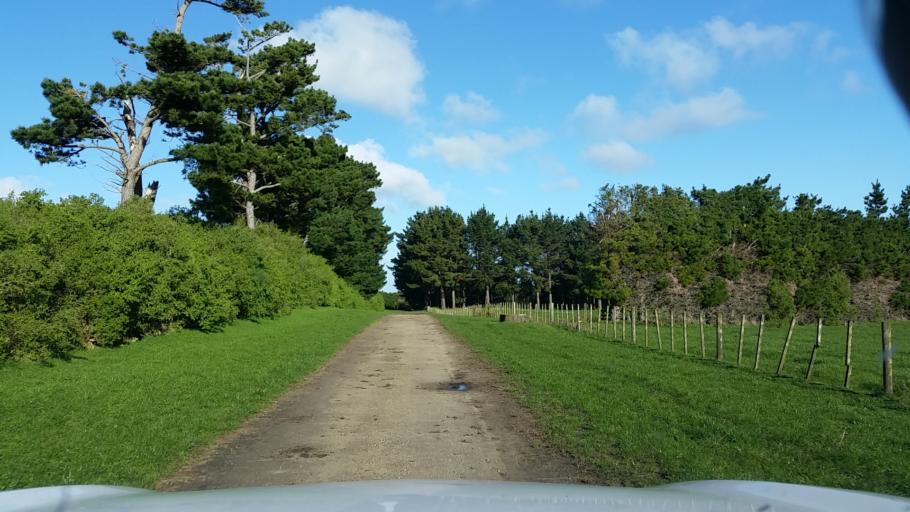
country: NZ
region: Taranaki
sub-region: South Taranaki District
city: Patea
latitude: -39.7408
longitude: 174.5434
